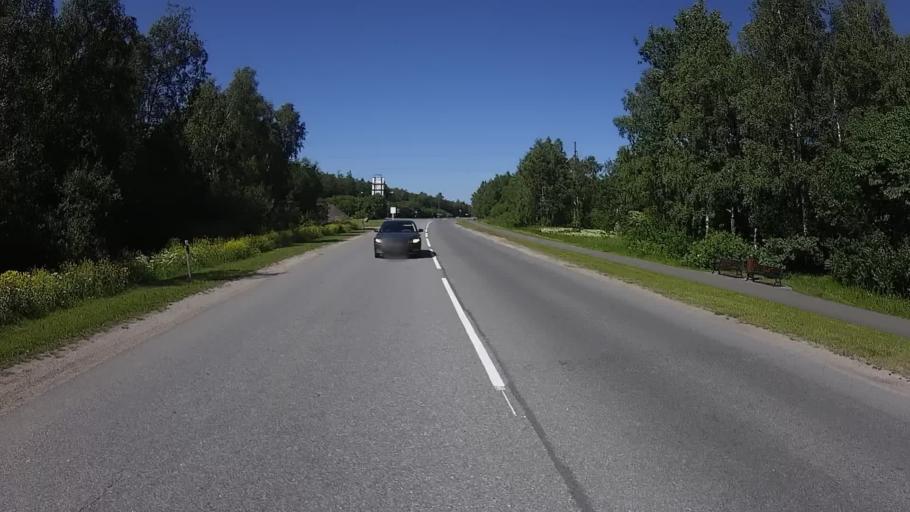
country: EE
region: Ida-Virumaa
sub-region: Kohtla-Jaerve linn
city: Kohtla-Jarve
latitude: 59.4129
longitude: 27.2765
